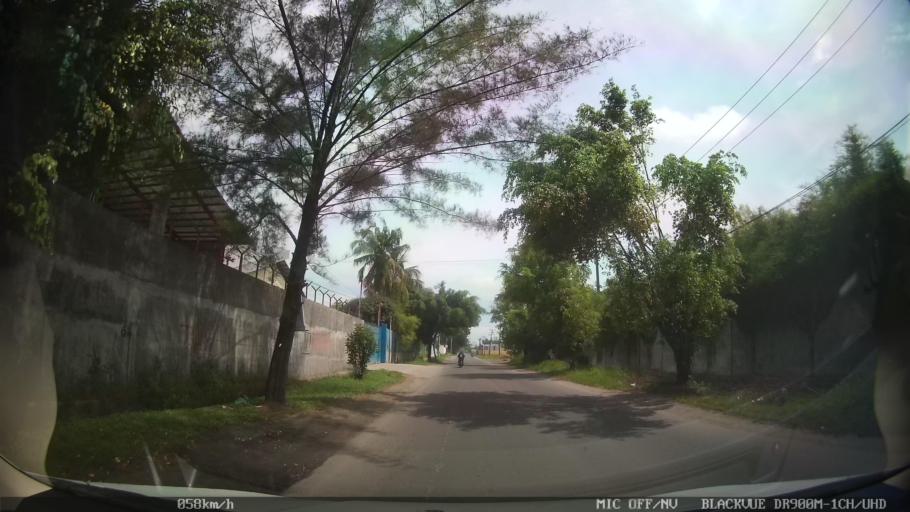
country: ID
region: North Sumatra
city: Medan
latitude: 3.6445
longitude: 98.7167
